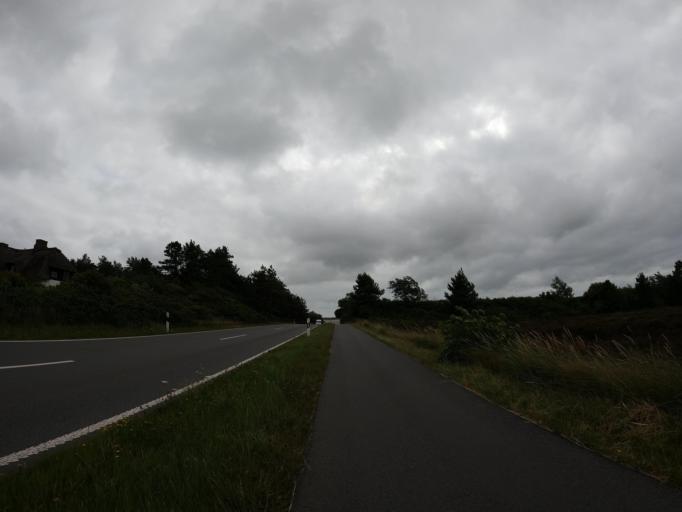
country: DE
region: Schleswig-Holstein
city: Keitum
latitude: 54.9225
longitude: 8.3589
